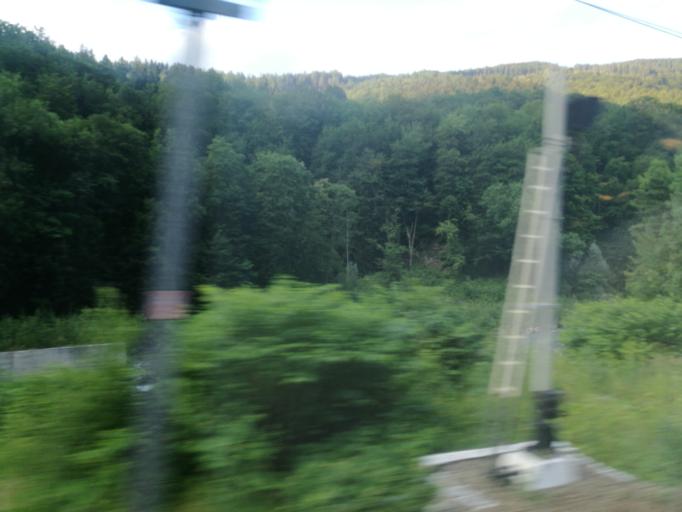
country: RO
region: Prahova
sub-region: Comuna Comarnic
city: Posada
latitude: 45.3035
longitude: 25.5775
